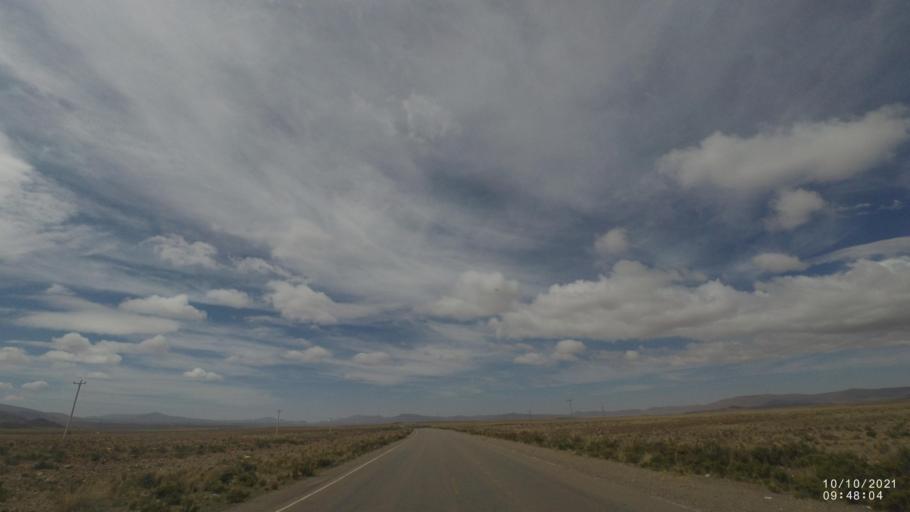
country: BO
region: La Paz
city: Quime
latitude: -17.2036
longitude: -67.3423
